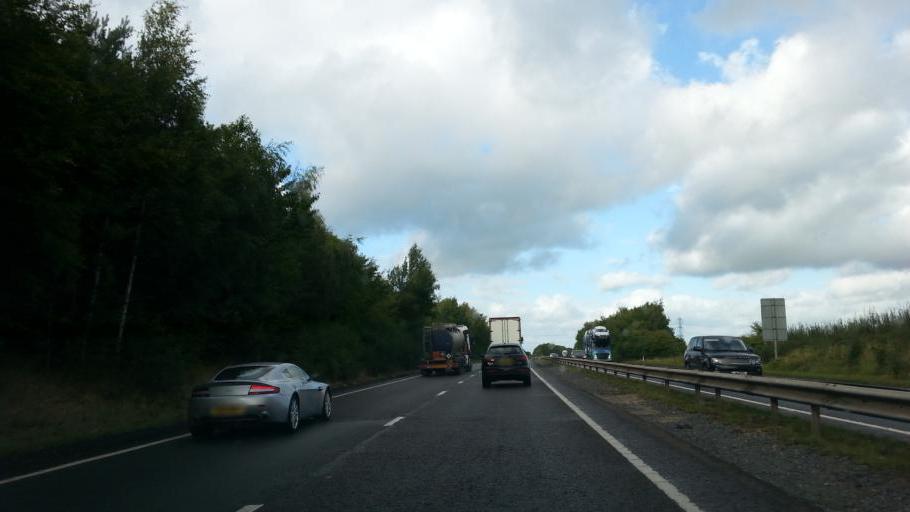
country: GB
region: England
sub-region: Derbyshire
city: Melbourne
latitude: 52.7840
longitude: -1.4138
